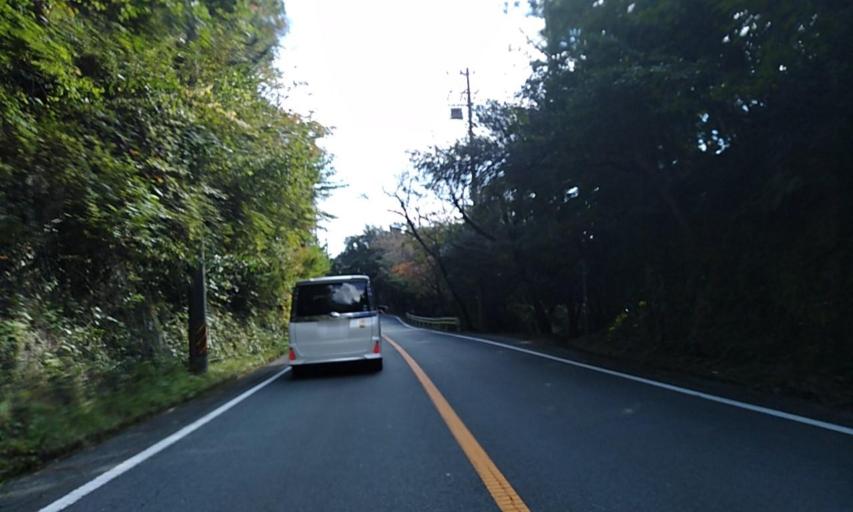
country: JP
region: Mie
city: Owase
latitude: 34.2203
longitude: 136.3931
